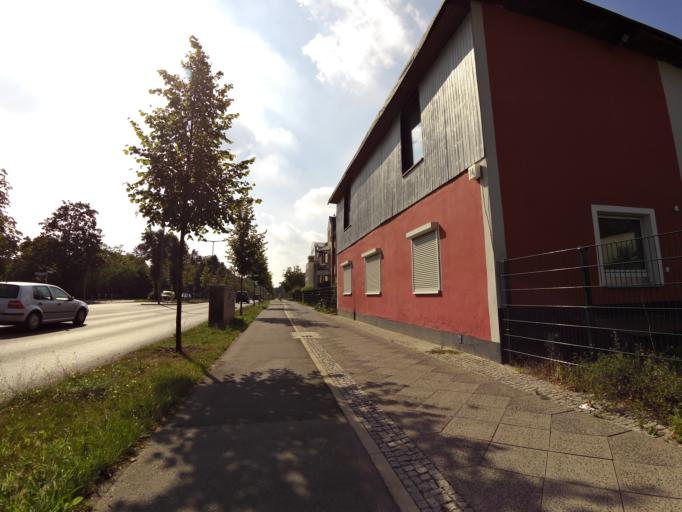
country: DE
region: Berlin
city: Lichtenrade
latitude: 52.3859
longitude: 13.4108
